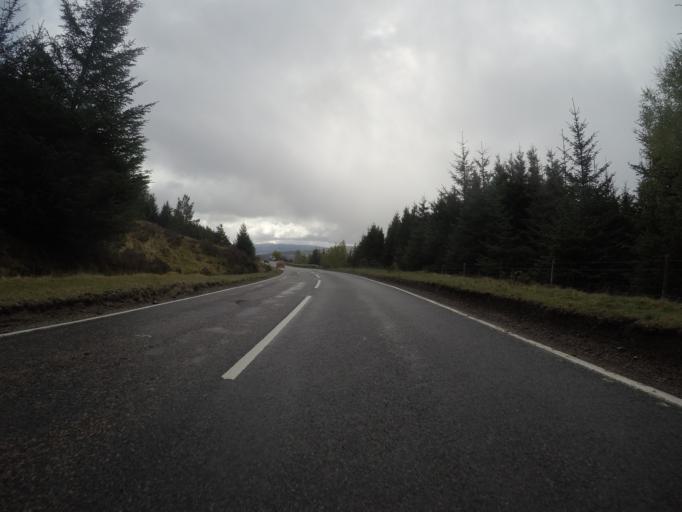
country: GB
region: Scotland
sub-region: Highland
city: Spean Bridge
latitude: 57.0825
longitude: -4.9555
